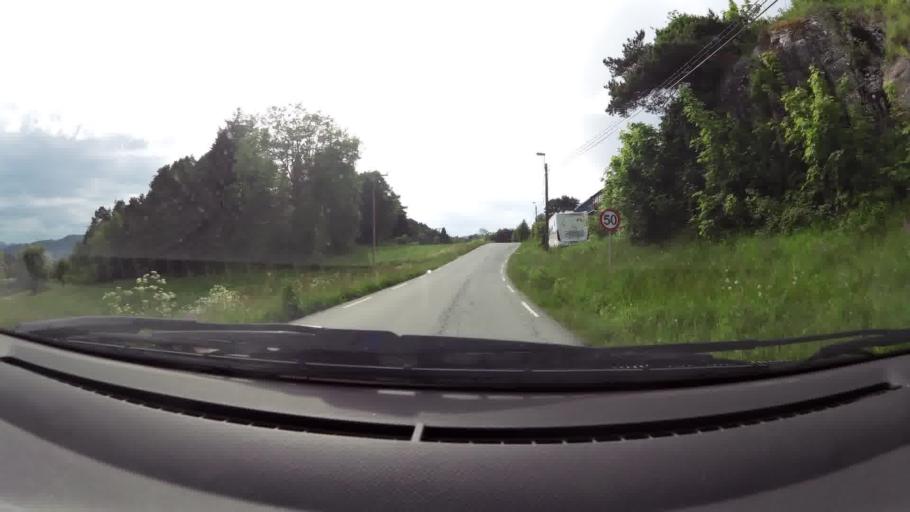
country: NO
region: More og Romsdal
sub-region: Kristiansund
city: Kristiansund
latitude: 63.0286
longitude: 7.7590
